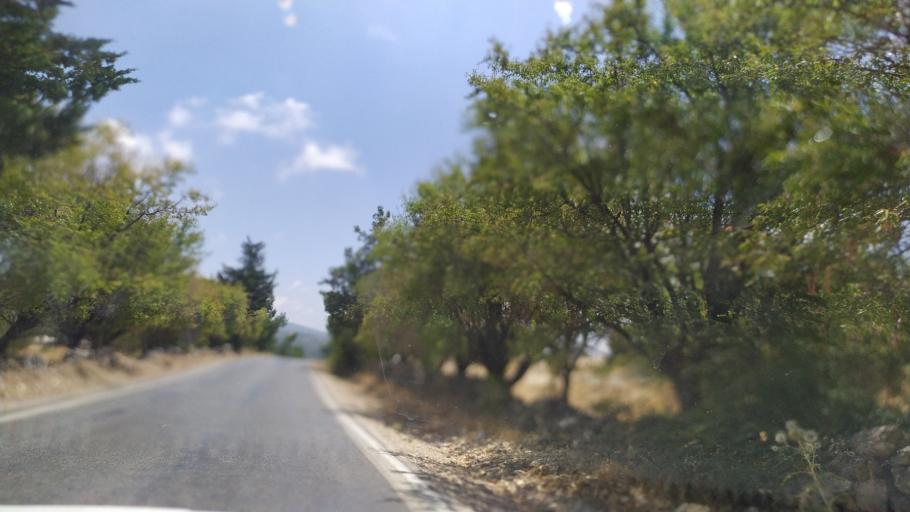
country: TR
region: Mersin
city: Gulnar
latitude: 36.2824
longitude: 33.3882
